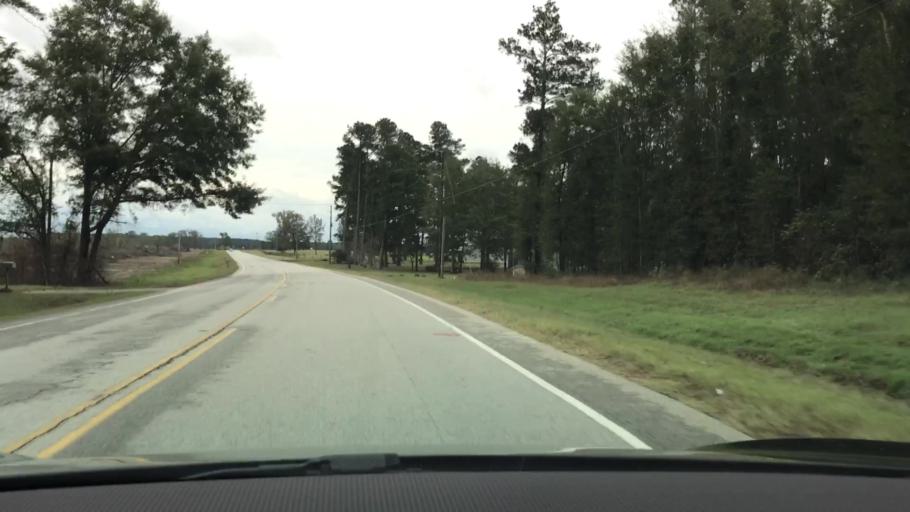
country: US
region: Georgia
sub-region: Jefferson County
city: Wrens
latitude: 33.1241
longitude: -82.4486
